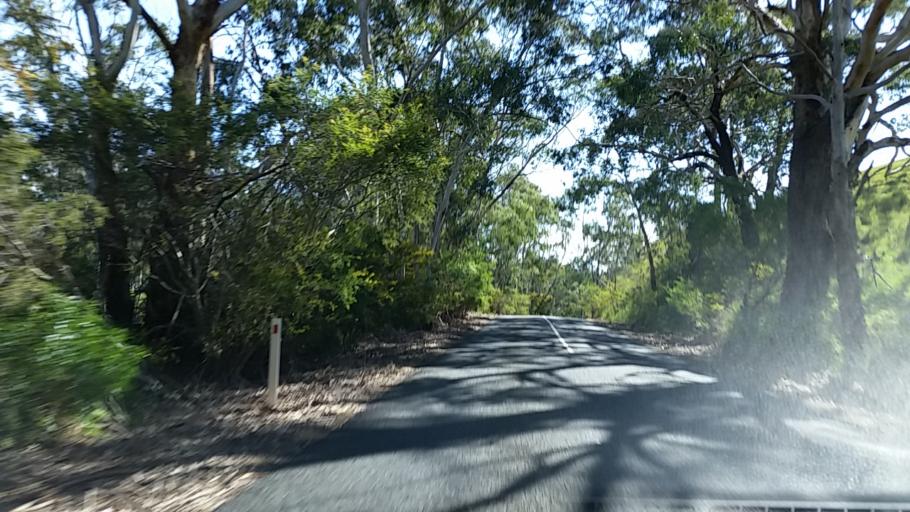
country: AU
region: South Australia
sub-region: Mount Barker
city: Hahndorf
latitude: -35.0772
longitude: 138.8091
